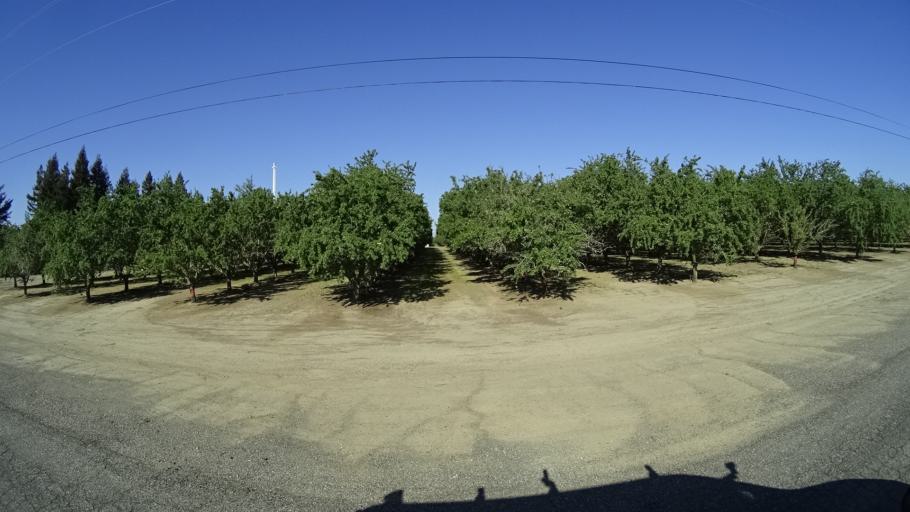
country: US
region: California
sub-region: Glenn County
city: Hamilton City
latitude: 39.7007
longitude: -122.0547
